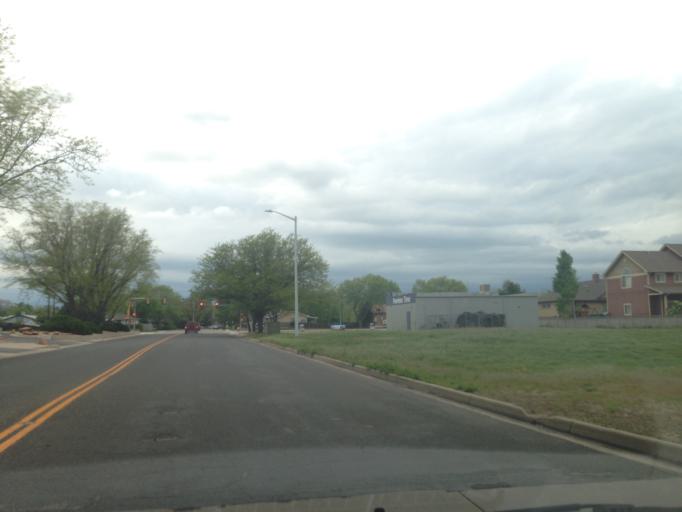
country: US
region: Colorado
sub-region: Boulder County
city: Longmont
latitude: 40.1411
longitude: -105.1008
